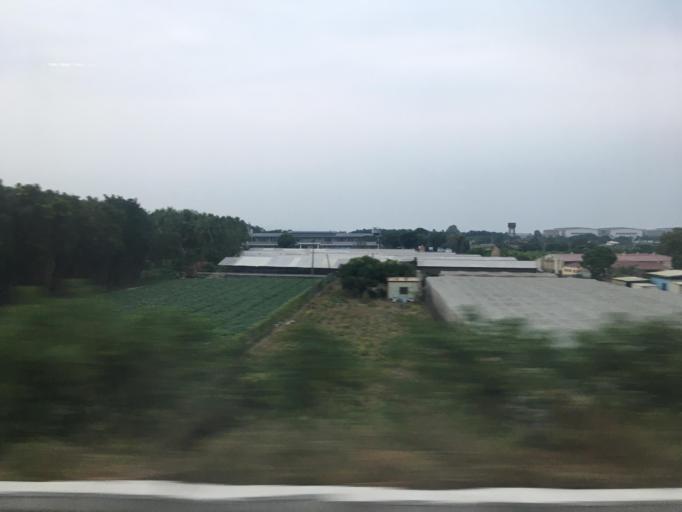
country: TW
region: Taiwan
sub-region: Pingtung
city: Pingtung
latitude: 22.6619
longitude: 120.4468
